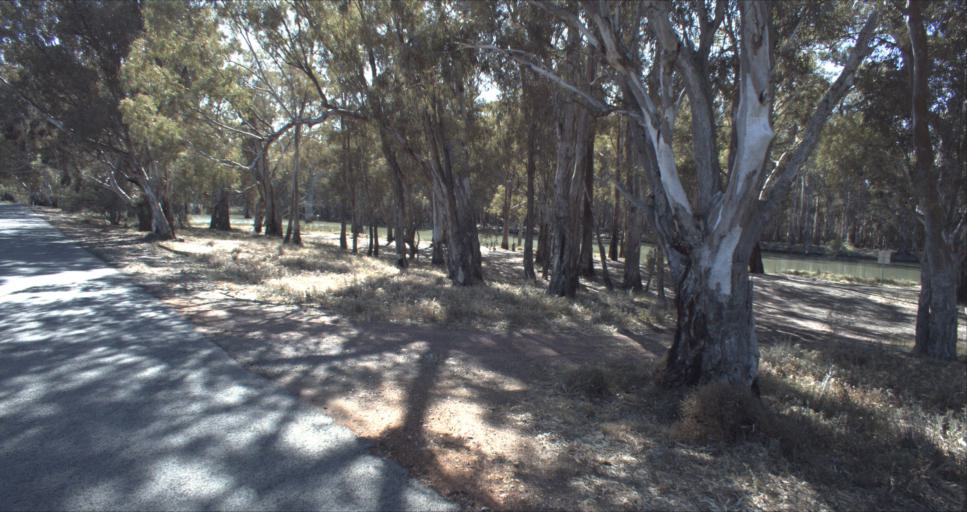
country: AU
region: New South Wales
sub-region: Leeton
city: Leeton
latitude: -34.6083
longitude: 146.2619
